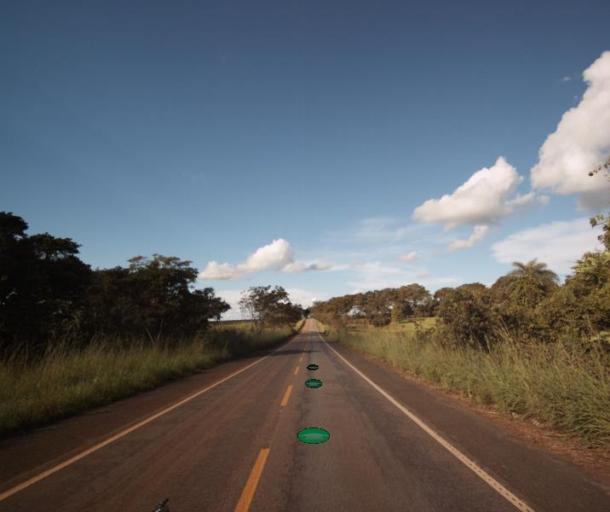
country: BR
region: Goias
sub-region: Itaberai
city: Itaberai
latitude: -15.9792
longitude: -49.6852
